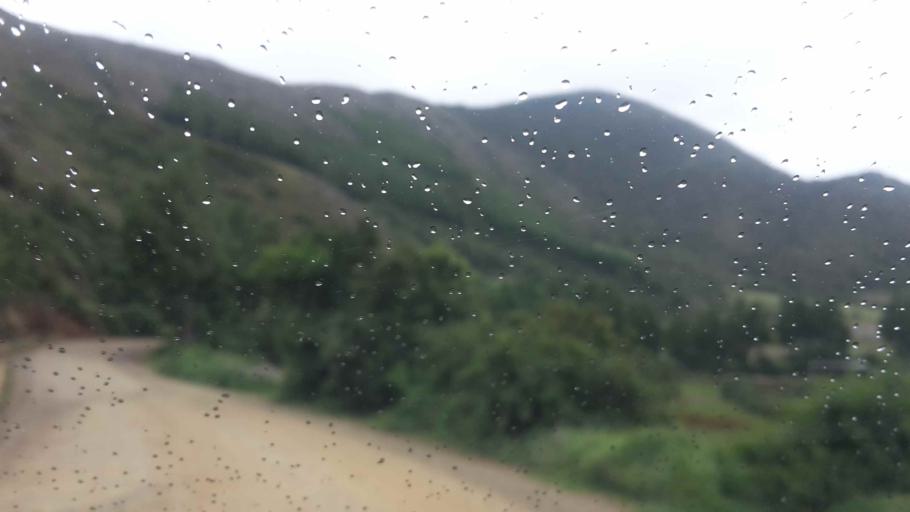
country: BO
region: Cochabamba
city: Totora
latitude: -17.5791
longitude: -65.2883
